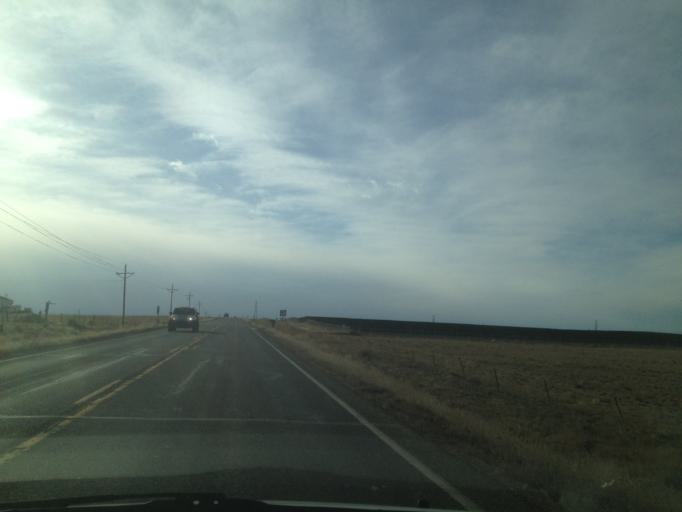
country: US
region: Colorado
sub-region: Weld County
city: Aristocrat Ranchettes
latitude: 40.0803
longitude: -104.7424
